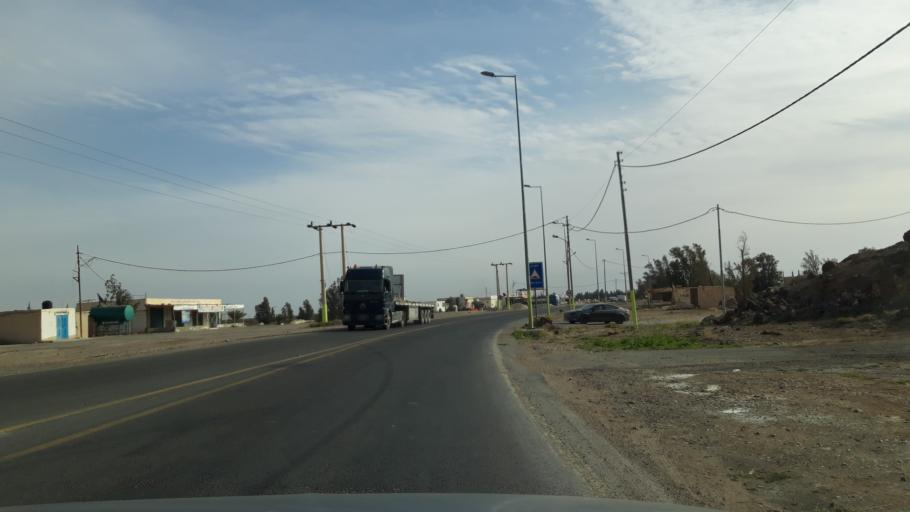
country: JO
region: Amman
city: Al Azraq ash Shamali
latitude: 31.8751
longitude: 36.8257
